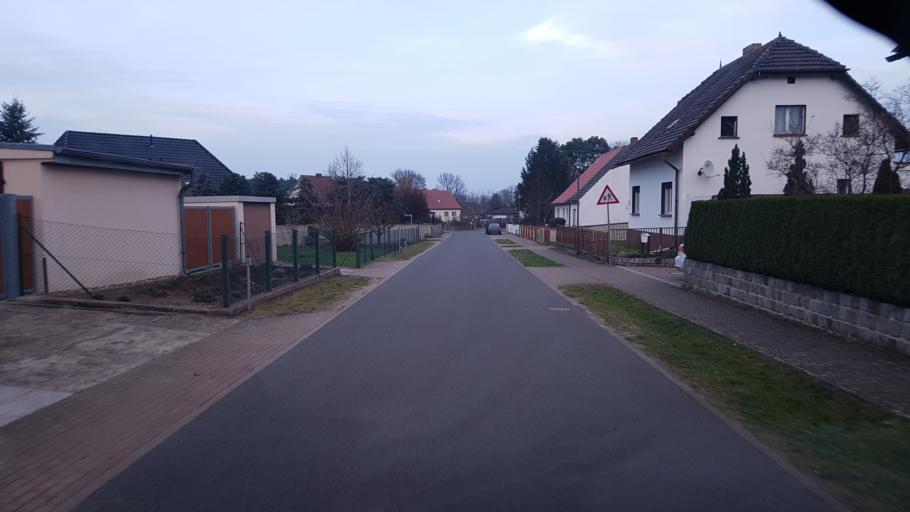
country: DE
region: Brandenburg
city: Ziltendorf
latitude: 52.2037
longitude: 14.6192
